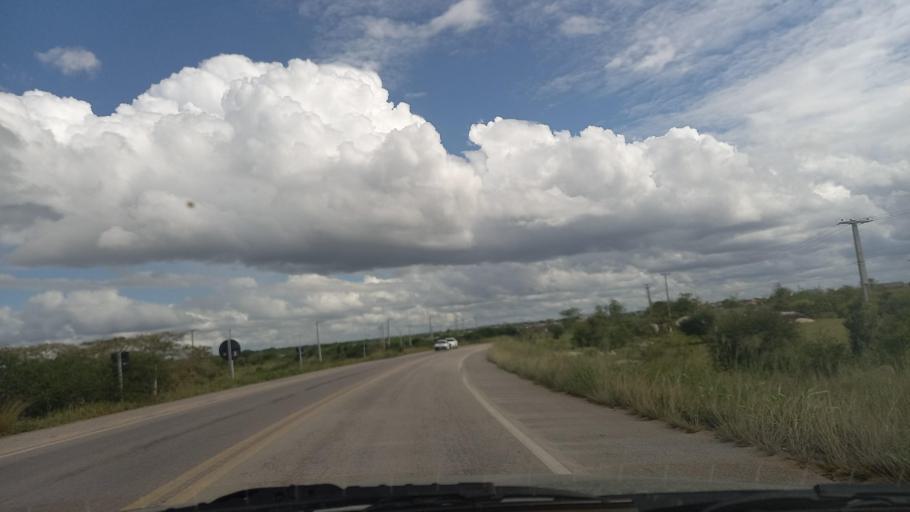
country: BR
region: Pernambuco
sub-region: Cachoeirinha
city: Cachoeirinha
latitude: -8.4830
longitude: -36.2254
